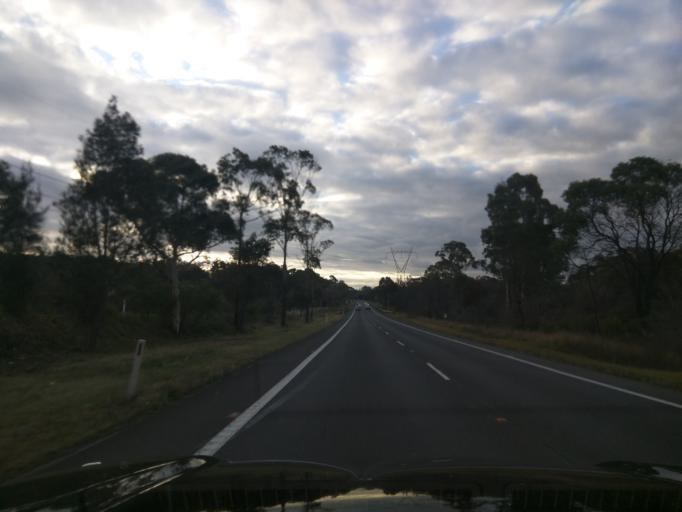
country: AU
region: New South Wales
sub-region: Wollondilly
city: Douglas Park
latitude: -34.2993
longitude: 150.7359
